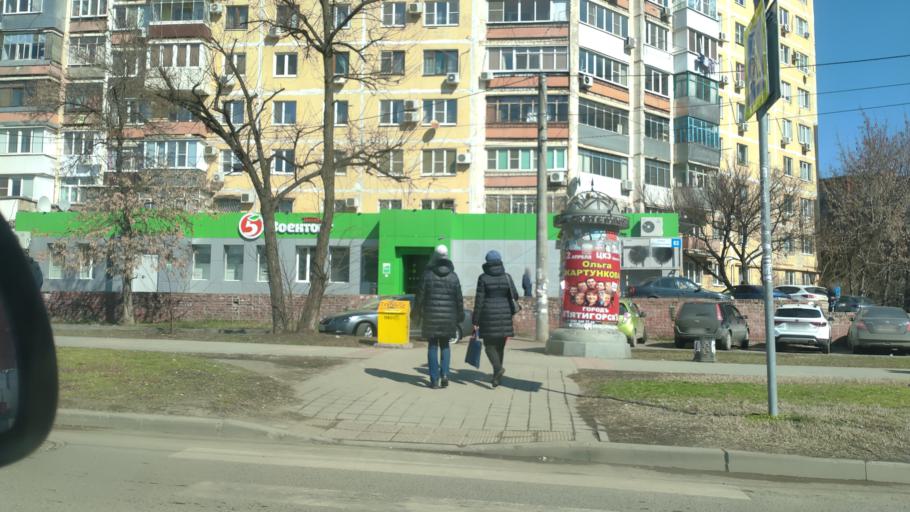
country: RU
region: Krasnodarskiy
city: Krasnodar
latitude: 45.0558
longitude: 39.0180
